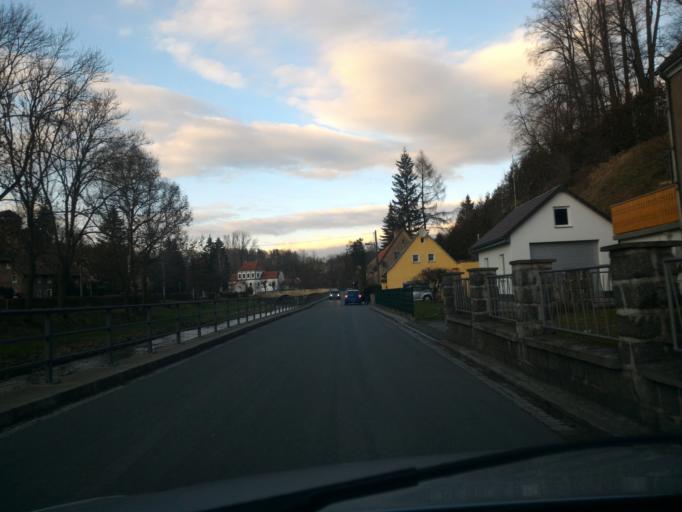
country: DE
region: Saxony
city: Hainewalde
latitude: 50.9130
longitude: 14.7086
